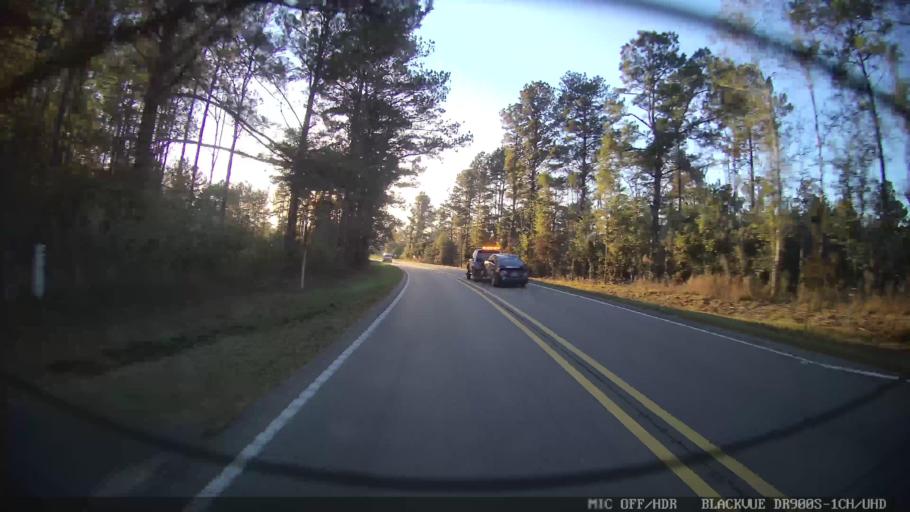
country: US
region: Mississippi
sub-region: Lamar County
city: Lumberton
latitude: 30.9971
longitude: -89.3664
